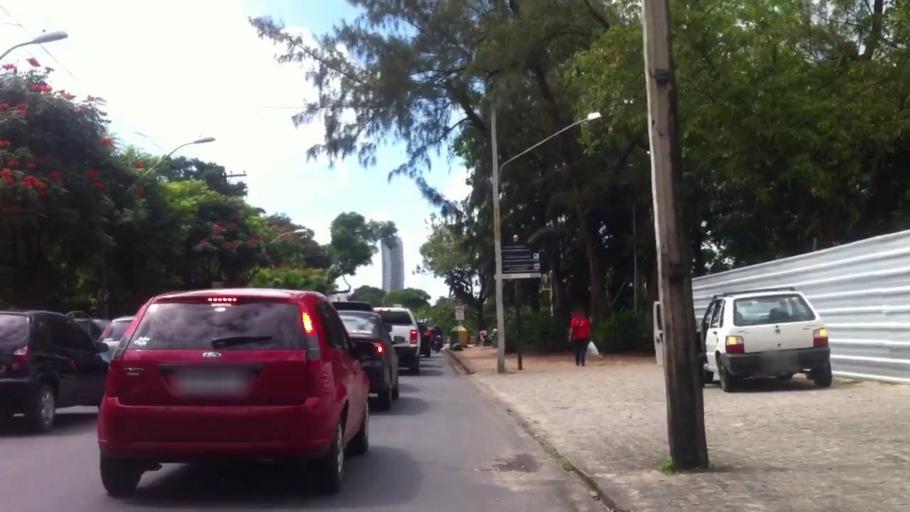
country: BR
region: Pernambuco
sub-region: Recife
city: Recife
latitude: -8.0377
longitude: -34.9058
